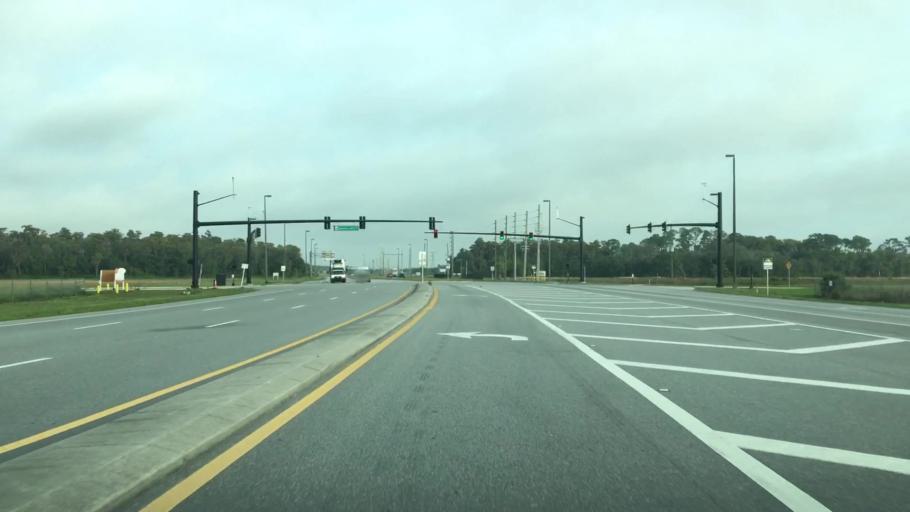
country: US
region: Florida
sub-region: Orange County
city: Conway
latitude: 28.4571
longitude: -81.2859
